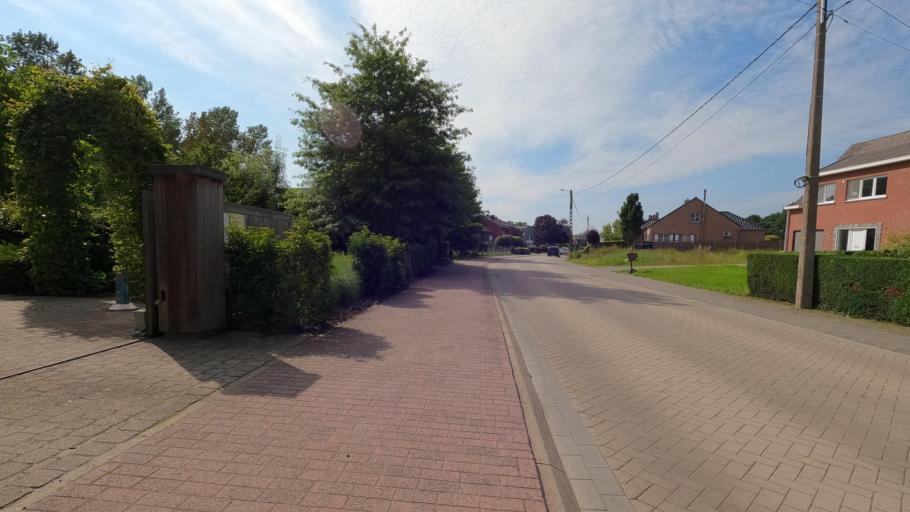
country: BE
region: Flanders
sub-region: Provincie Antwerpen
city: Heist-op-den-Berg
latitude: 51.0674
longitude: 4.7113
